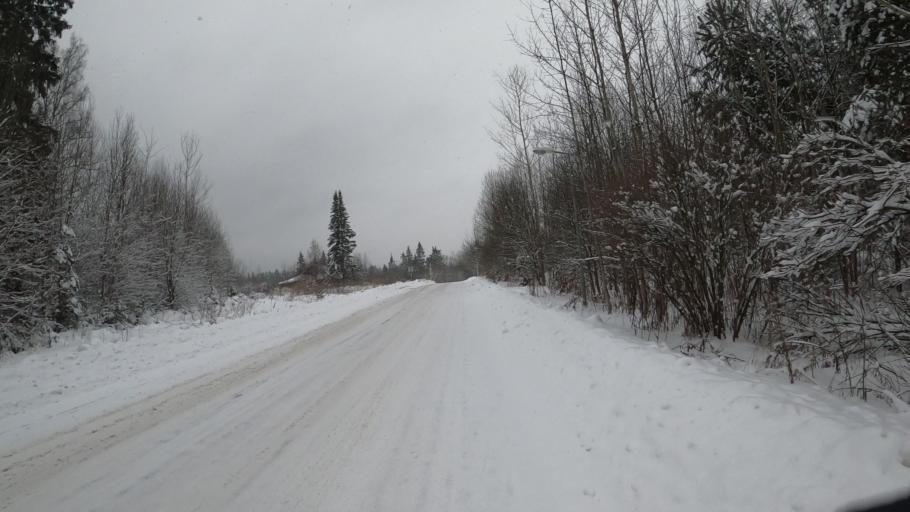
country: RU
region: Moskovskaya
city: Firsanovka
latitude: 55.9193
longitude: 37.2096
